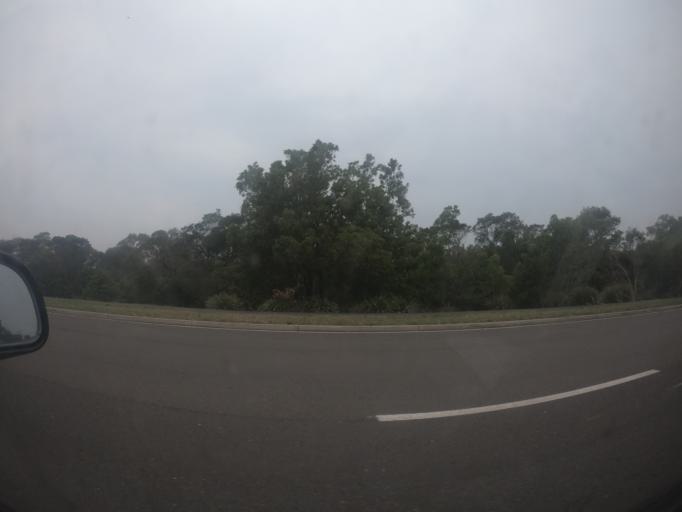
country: AU
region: New South Wales
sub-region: Shellharbour
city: Flinders
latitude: -34.5945
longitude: 150.8545
